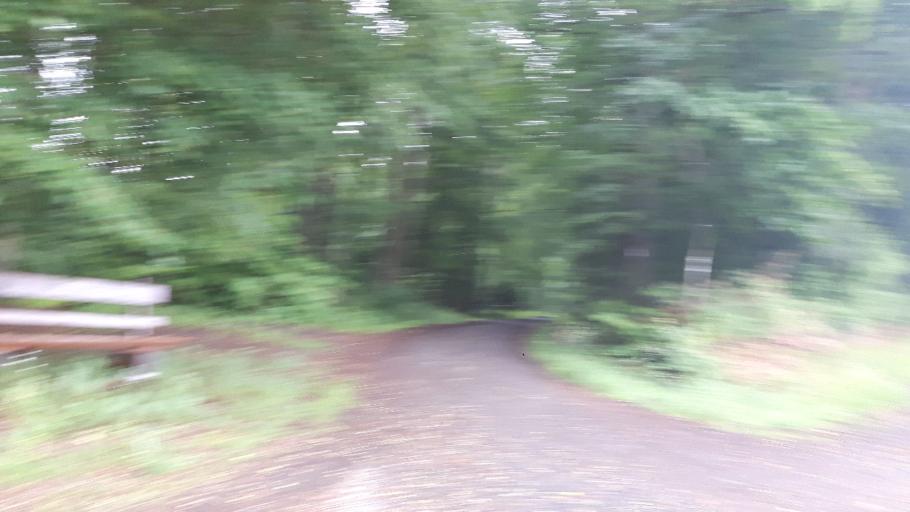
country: DE
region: Bavaria
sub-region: Regierungsbezirk Unterfranken
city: Uchtelhausen
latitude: 50.1219
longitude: 10.3246
